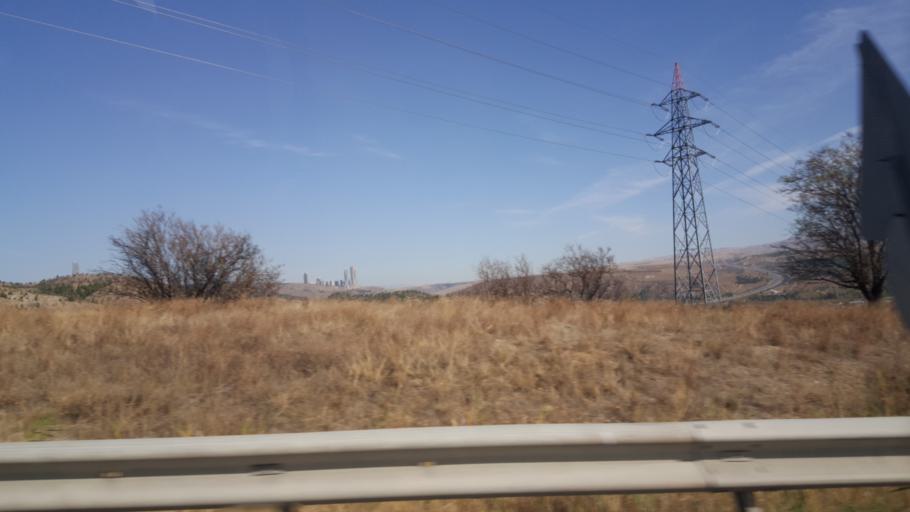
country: TR
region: Ankara
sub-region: Goelbasi
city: Golbasi
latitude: 39.8114
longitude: 32.7993
